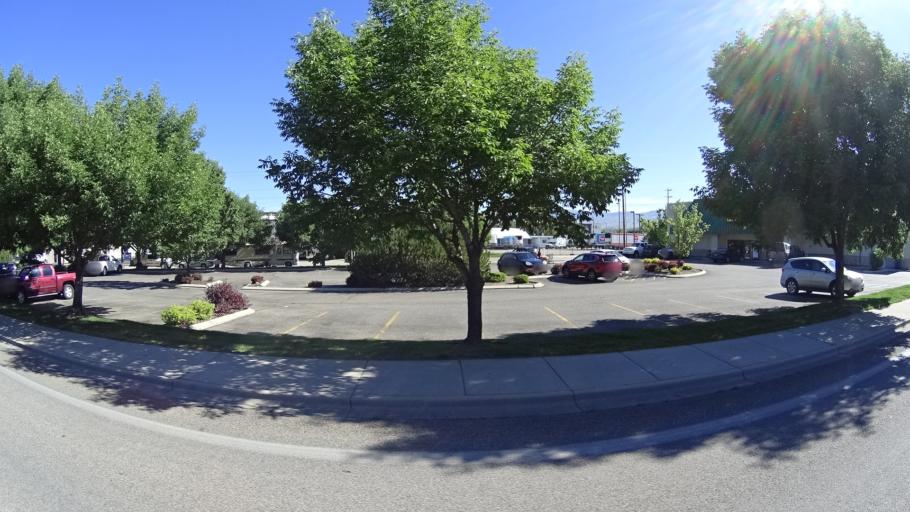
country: US
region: Idaho
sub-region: Ada County
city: Garden City
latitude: 43.6176
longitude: -116.2223
